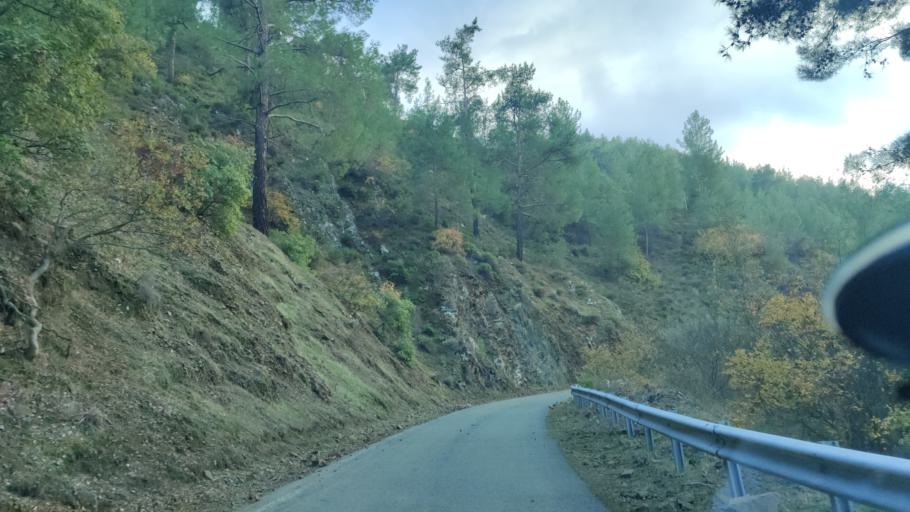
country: CY
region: Lefkosia
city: Lefka
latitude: 35.0708
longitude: 32.7423
